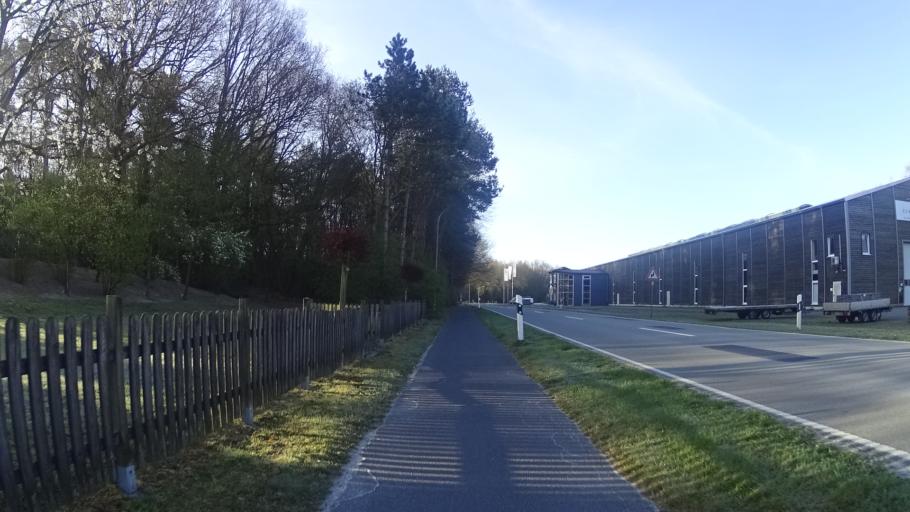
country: DE
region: Lower Saxony
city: Lathen
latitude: 52.8746
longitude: 7.3173
